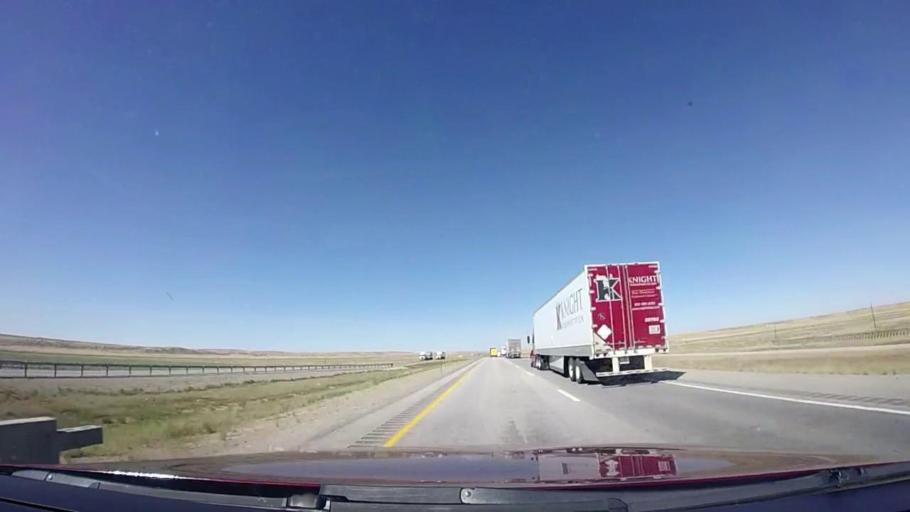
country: US
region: Wyoming
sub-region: Carbon County
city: Rawlins
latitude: 41.6655
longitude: -108.0326
